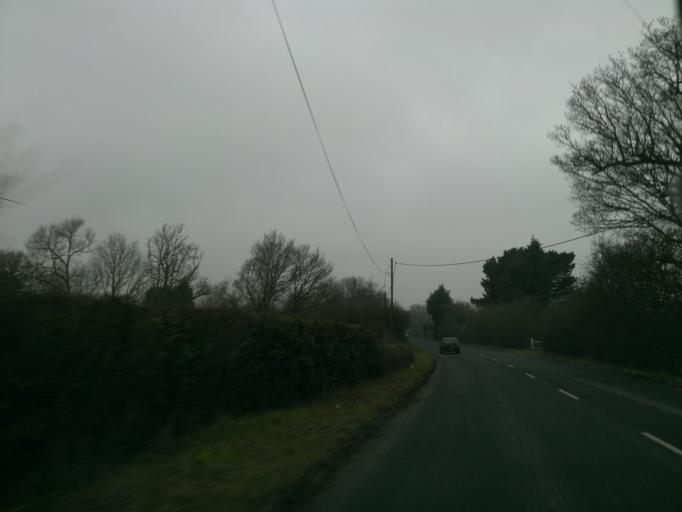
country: GB
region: England
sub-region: Essex
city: Alresford
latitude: 51.8815
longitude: 1.0198
